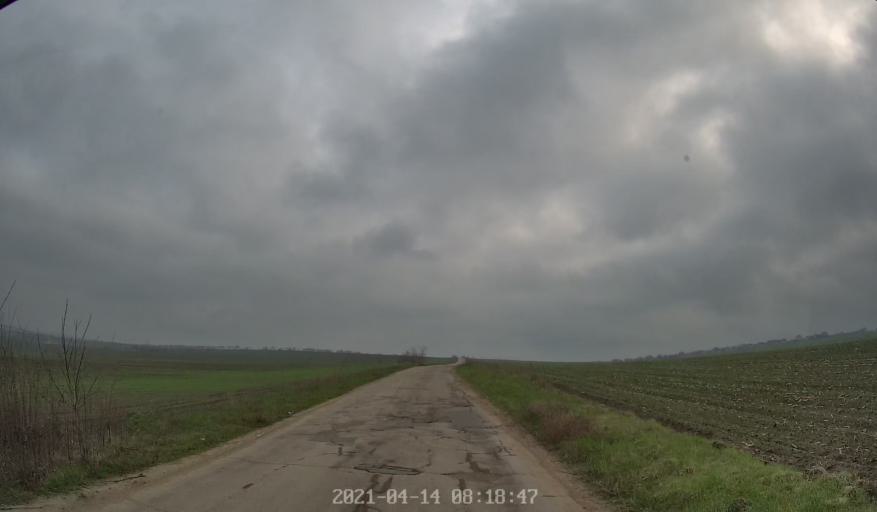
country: MD
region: Chisinau
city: Stauceni
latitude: 47.0575
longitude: 28.9177
